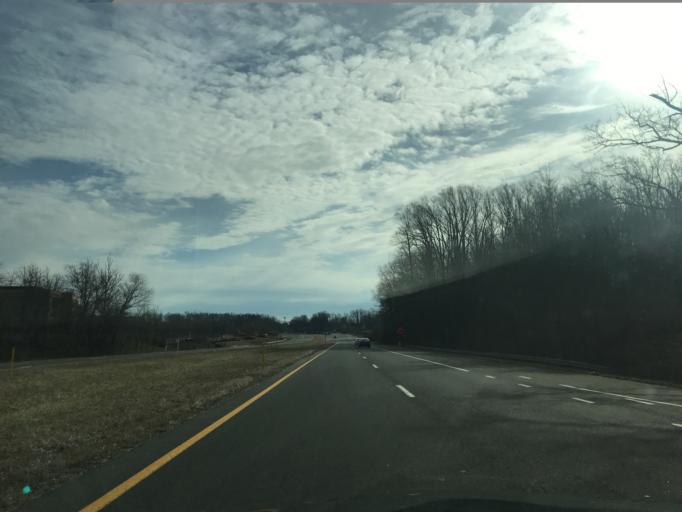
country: US
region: Maryland
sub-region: Prince George's County
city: Glenn Dale
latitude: 38.9664
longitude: -76.7970
